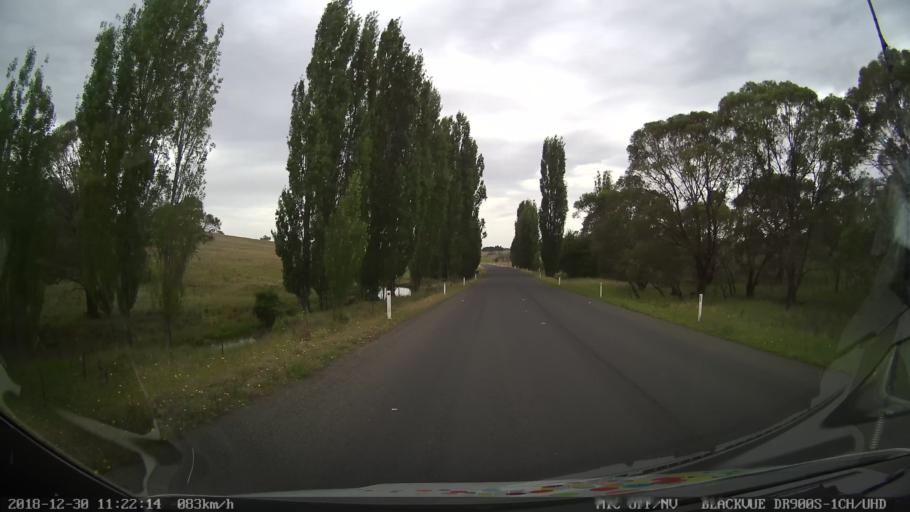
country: AU
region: New South Wales
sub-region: Snowy River
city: Jindabyne
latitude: -36.5023
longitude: 148.6706
